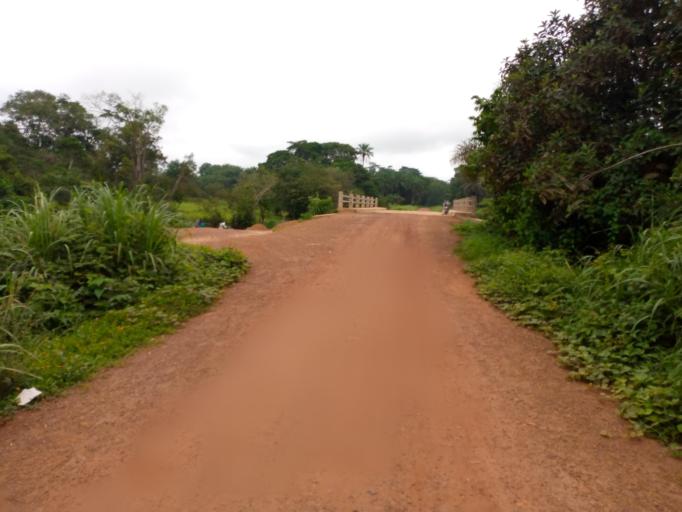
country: SL
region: Southern Province
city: Sumbuya
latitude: 7.5618
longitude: -12.0858
